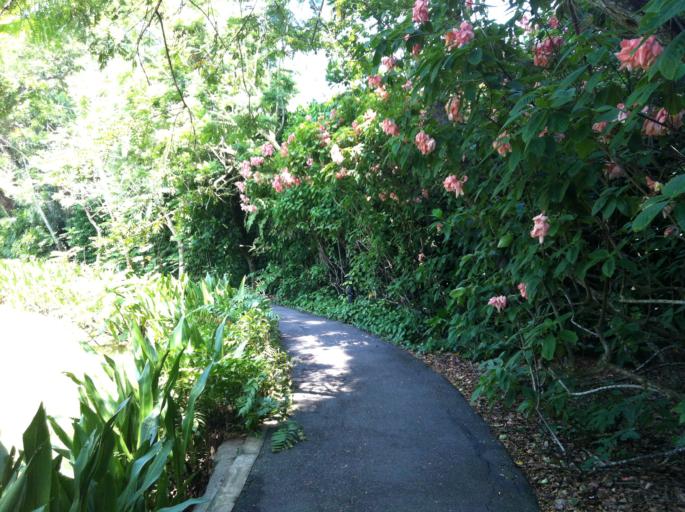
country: SG
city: Singapore
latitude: 1.3074
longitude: 103.8158
